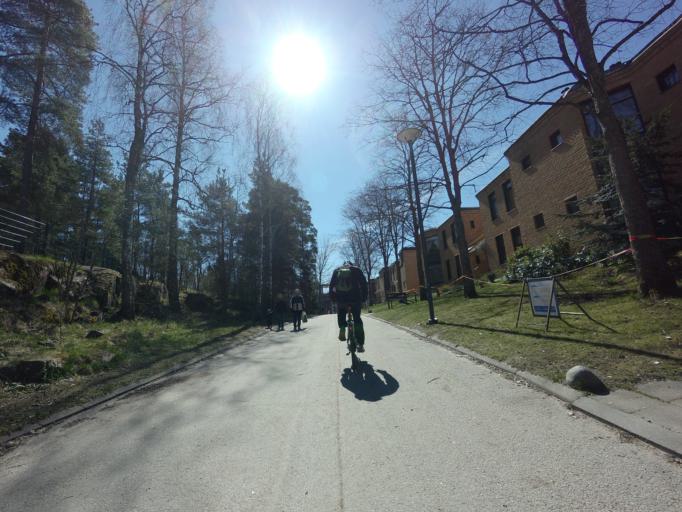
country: FI
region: Uusimaa
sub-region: Helsinki
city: Koukkuniemi
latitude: 60.1673
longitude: 24.7316
